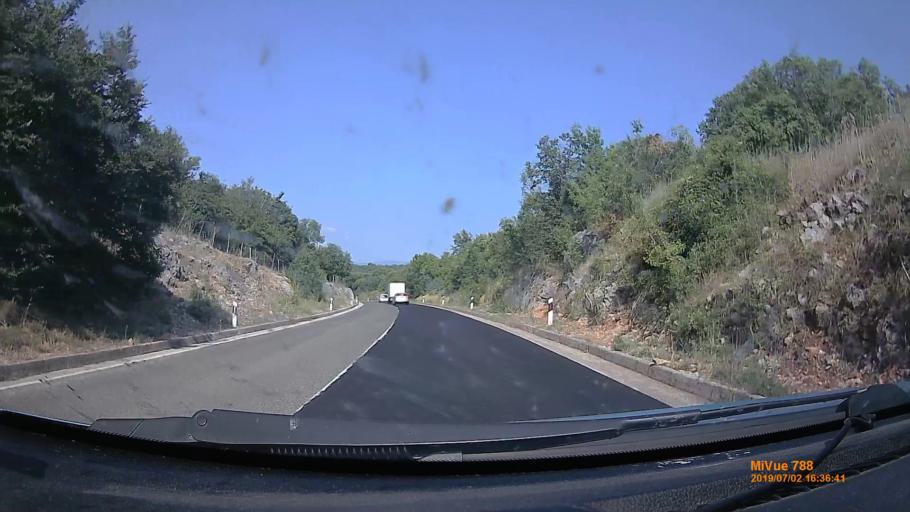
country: HR
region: Primorsko-Goranska
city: Njivice
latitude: 45.0906
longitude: 14.5291
